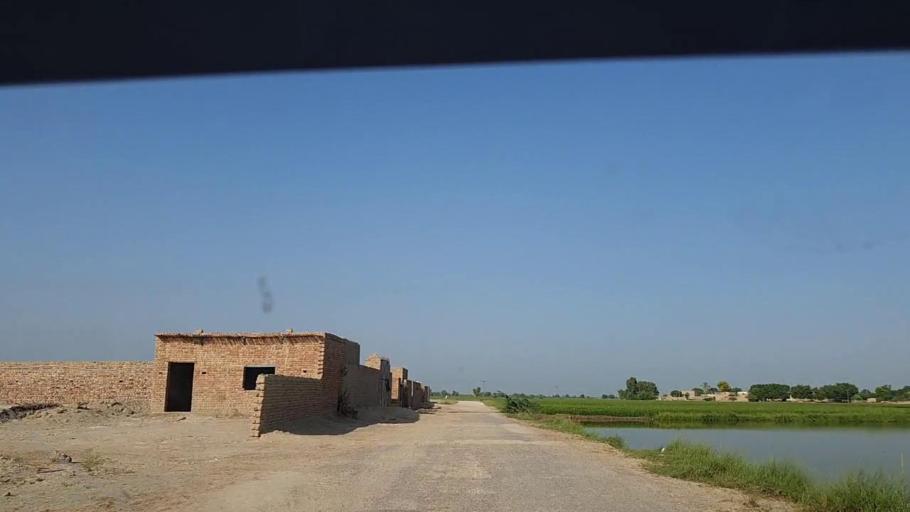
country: PK
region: Sindh
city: Tangwani
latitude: 28.2627
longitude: 69.0094
